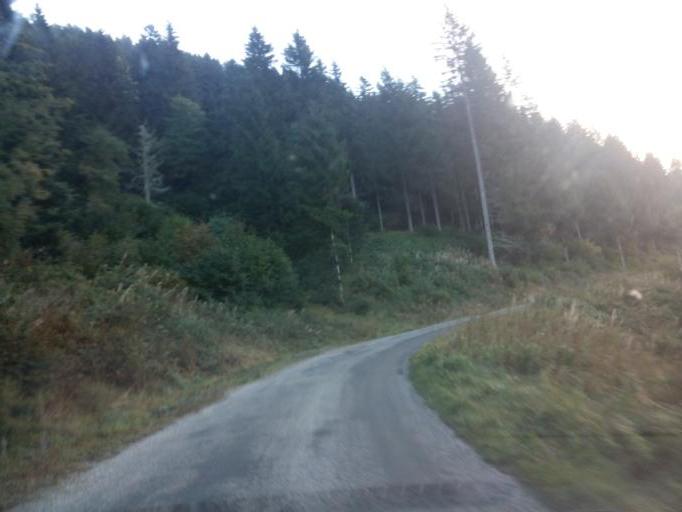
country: FR
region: Rhone-Alpes
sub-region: Departement de l'Isere
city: Theys
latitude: 45.2319
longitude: 5.9901
